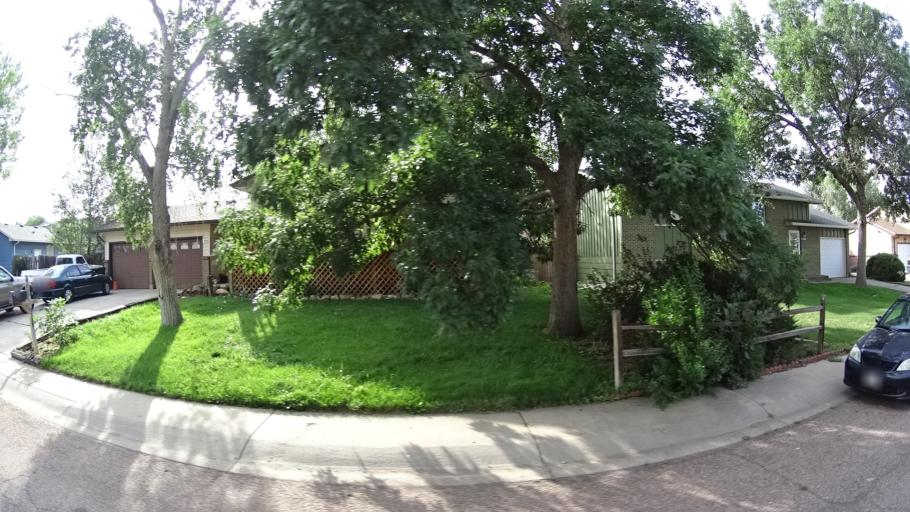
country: US
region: Colorado
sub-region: El Paso County
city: Security-Widefield
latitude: 38.7246
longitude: -104.7006
